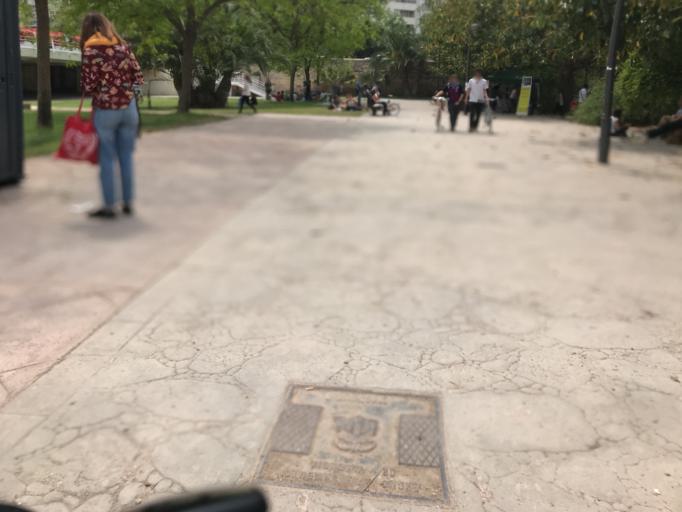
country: ES
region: Valencia
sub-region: Provincia de Valencia
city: Valencia
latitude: 39.4713
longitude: -0.3646
